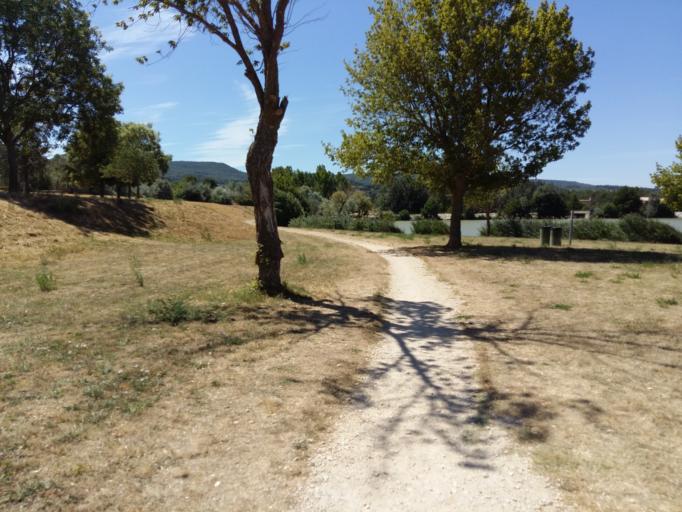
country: FR
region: Provence-Alpes-Cote d'Azur
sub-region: Departement du Vaucluse
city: Apt
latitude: 43.8902
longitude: 5.3807
